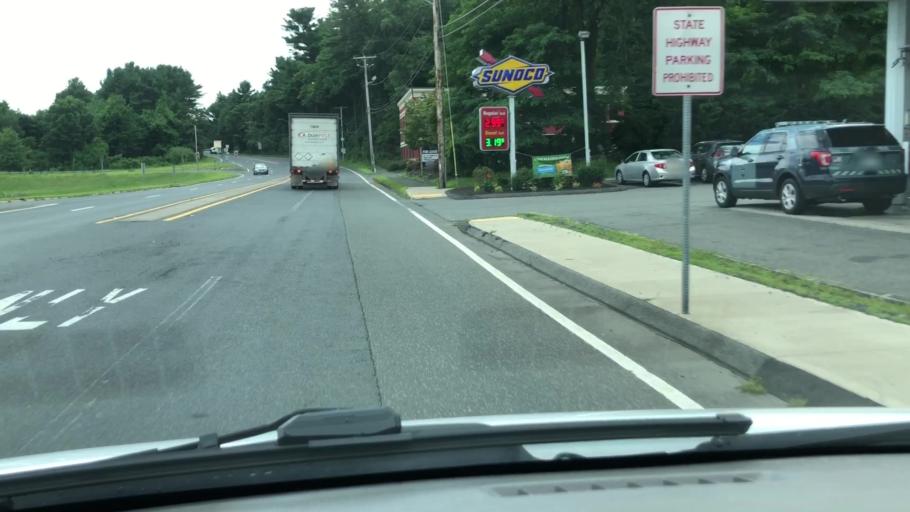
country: US
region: Massachusetts
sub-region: Hampshire County
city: Northampton
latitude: 42.3623
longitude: -72.6386
